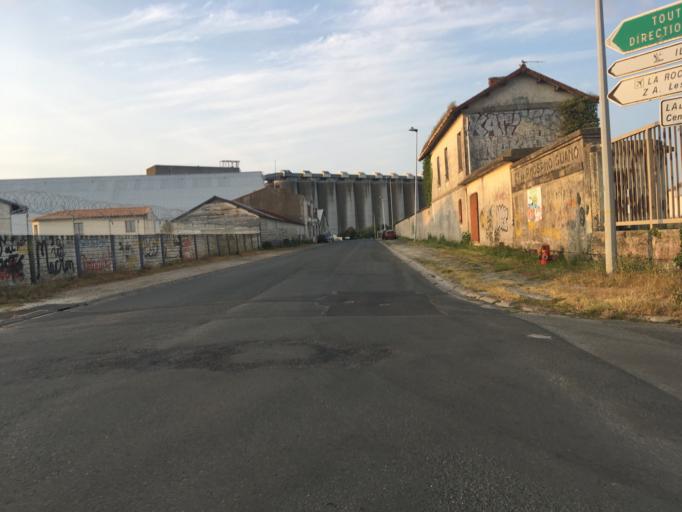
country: FR
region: Poitou-Charentes
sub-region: Departement de la Charente-Maritime
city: Rivedoux-Plage
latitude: 46.1634
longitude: -1.2183
